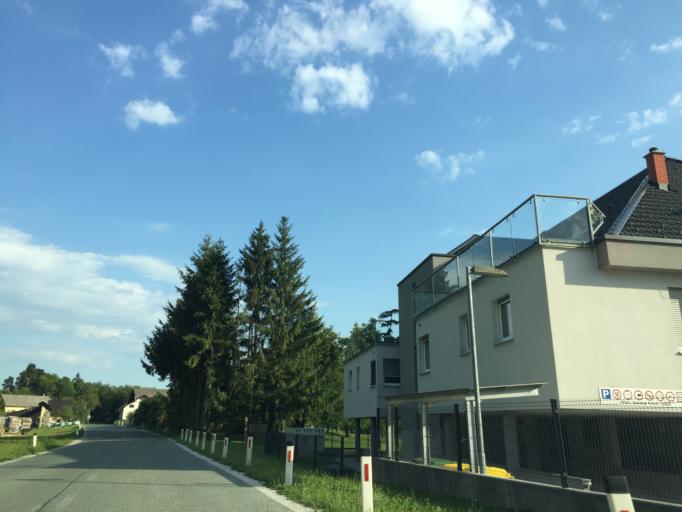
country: SI
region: Trzic
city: Bistrica pri Trzicu
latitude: 46.3110
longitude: 14.2406
